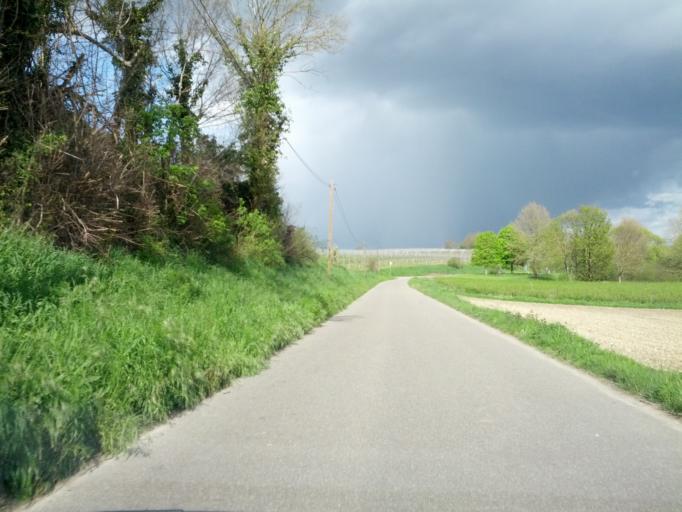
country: DE
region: Baden-Wuerttemberg
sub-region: Freiburg Region
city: Merdingen
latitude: 48.0035
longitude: 7.7040
